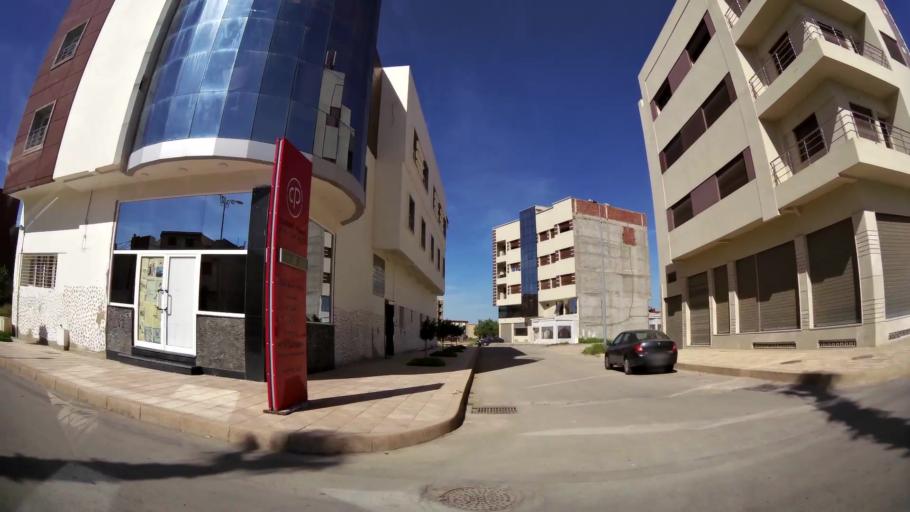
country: MA
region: Oriental
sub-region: Oujda-Angad
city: Oujda
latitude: 34.6667
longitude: -1.8971
